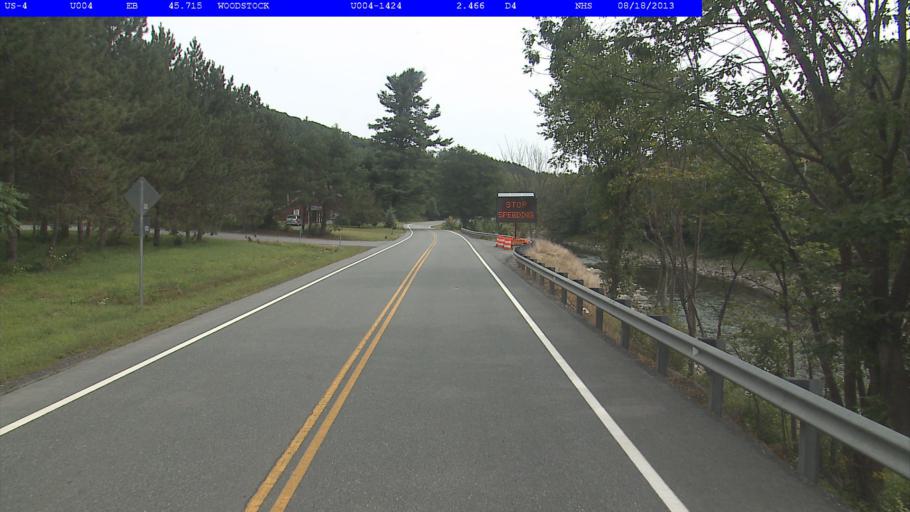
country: US
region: Vermont
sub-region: Windsor County
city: Woodstock
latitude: 43.5999
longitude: -72.5803
